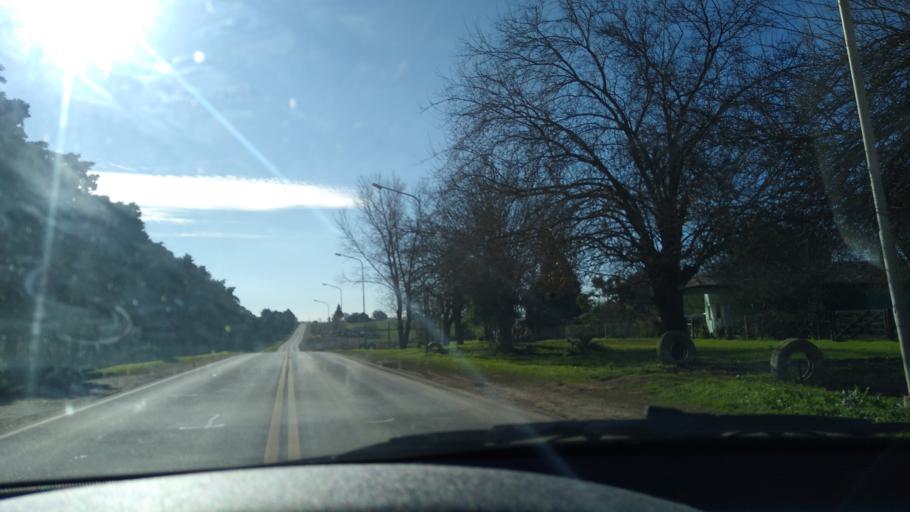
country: AR
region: Entre Rios
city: Aranguren
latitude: -32.4209
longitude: -60.3150
